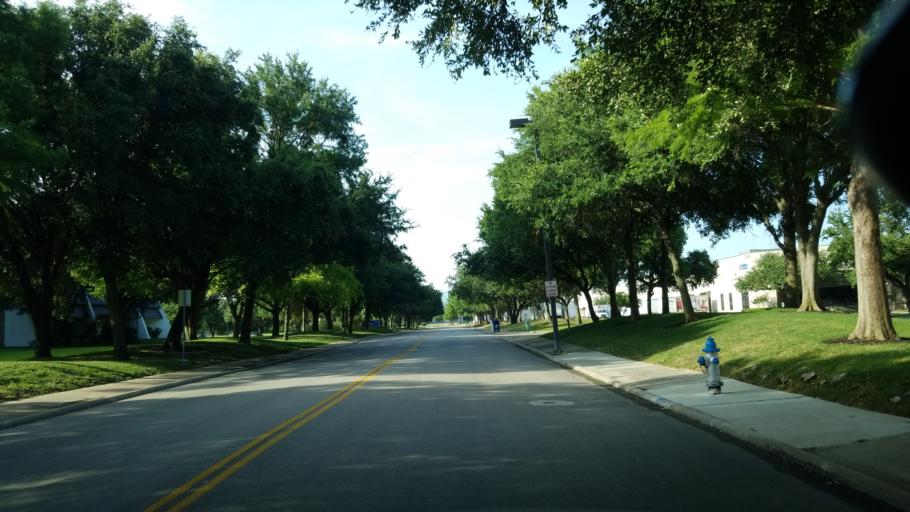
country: US
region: Texas
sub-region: Dallas County
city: Coppell
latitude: 32.9297
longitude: -97.0171
